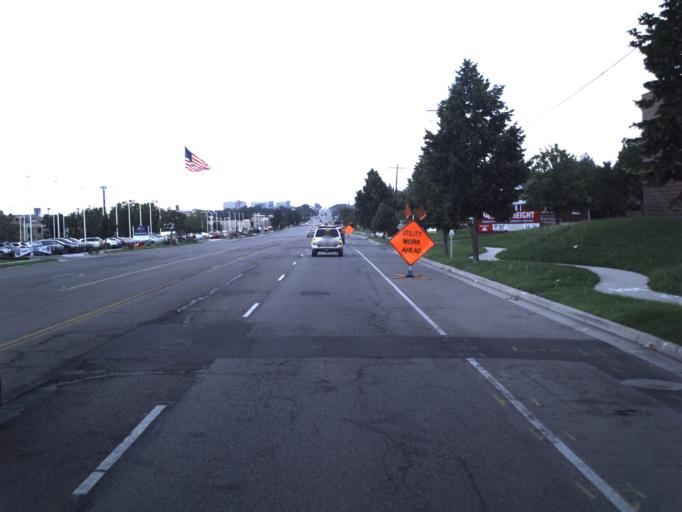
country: US
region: Utah
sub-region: Salt Lake County
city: White City
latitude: 40.5524
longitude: -111.8907
